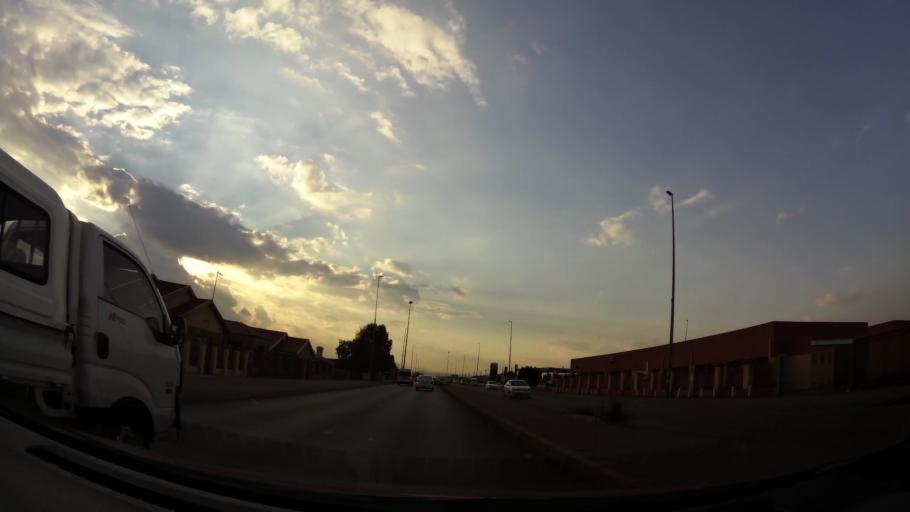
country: ZA
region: Gauteng
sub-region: City of Johannesburg Metropolitan Municipality
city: Orange Farm
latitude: -26.5694
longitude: 27.8367
